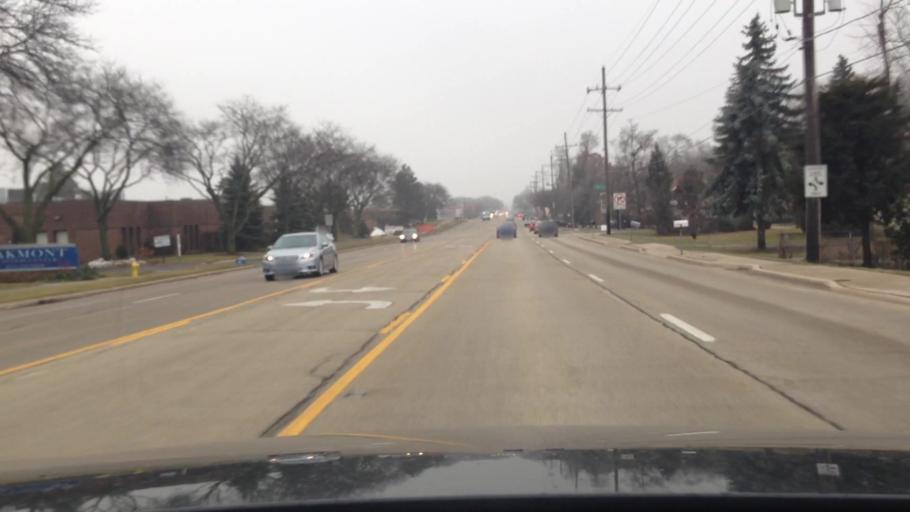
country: US
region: Illinois
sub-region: DuPage County
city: Westmont
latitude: 41.8158
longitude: -87.9761
